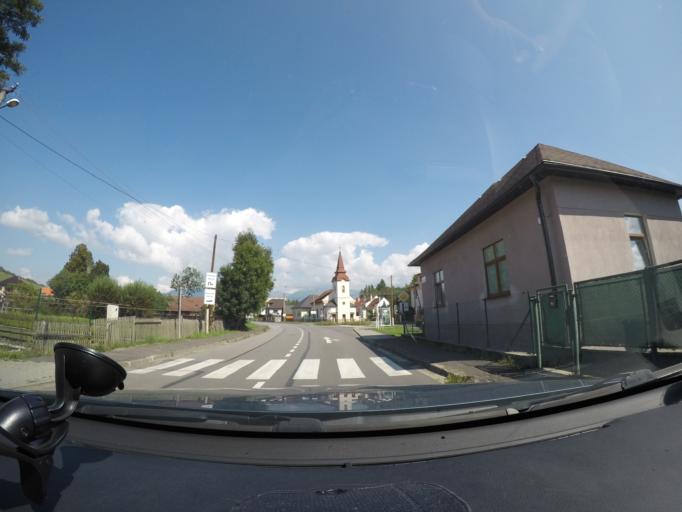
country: SK
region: Zilinsky
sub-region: Okres Liptovsky Mikulas
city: Liptovsky Mikulas
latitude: 49.0970
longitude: 19.5892
